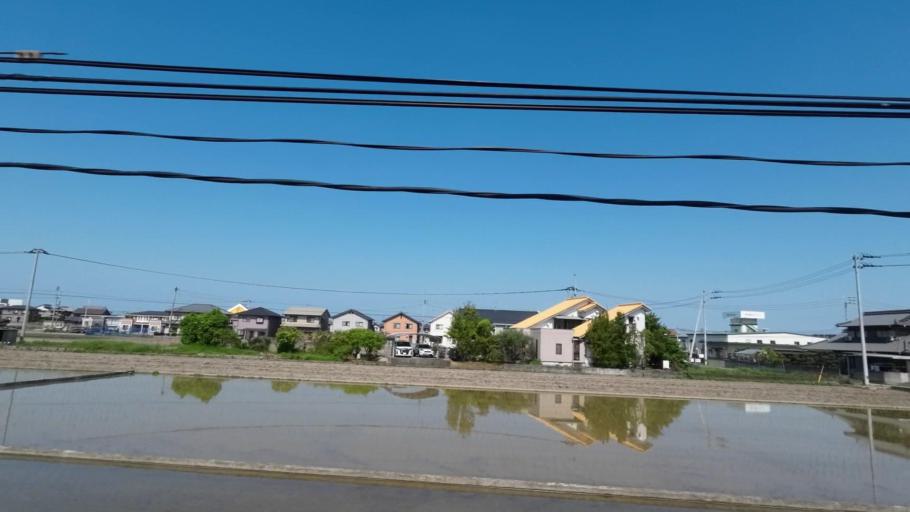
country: JP
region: Kagawa
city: Kan'onjicho
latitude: 34.1205
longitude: 133.6478
